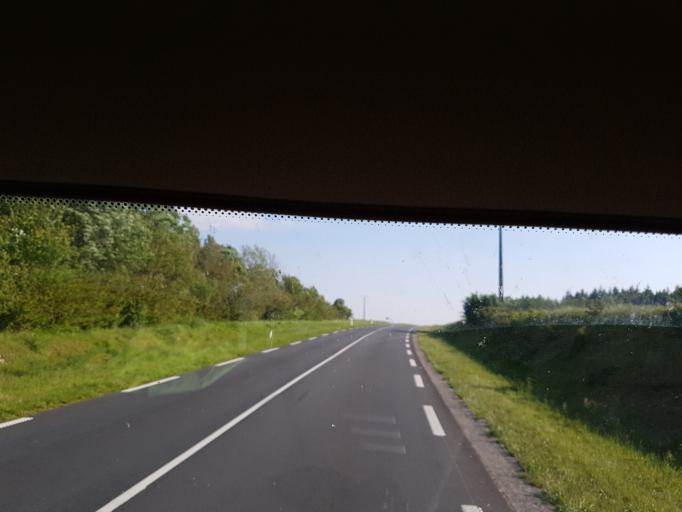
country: FR
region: Picardie
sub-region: Departement de la Somme
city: Crecy-en-Ponthieu
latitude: 50.1787
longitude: 1.8719
